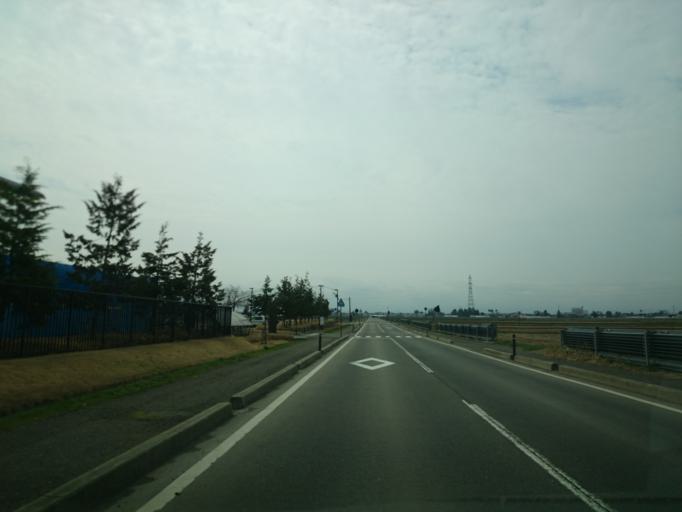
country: JP
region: Fukushima
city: Inawashiro
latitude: 37.5614
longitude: 140.0995
